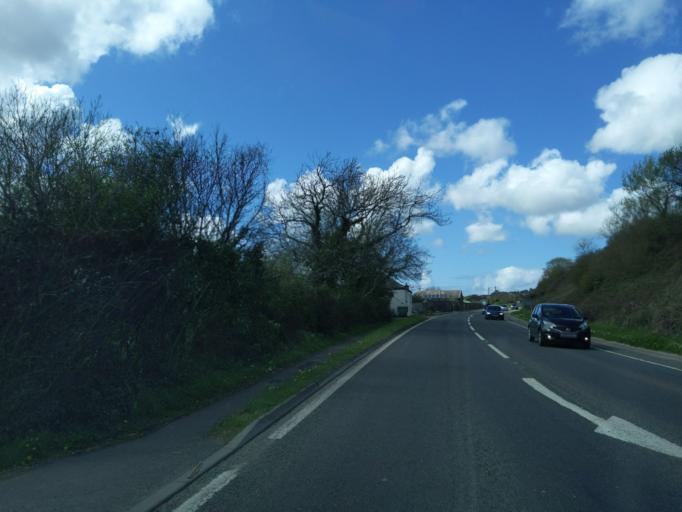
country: GB
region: England
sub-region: Cornwall
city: Wadebridge
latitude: 50.5101
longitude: -4.8135
